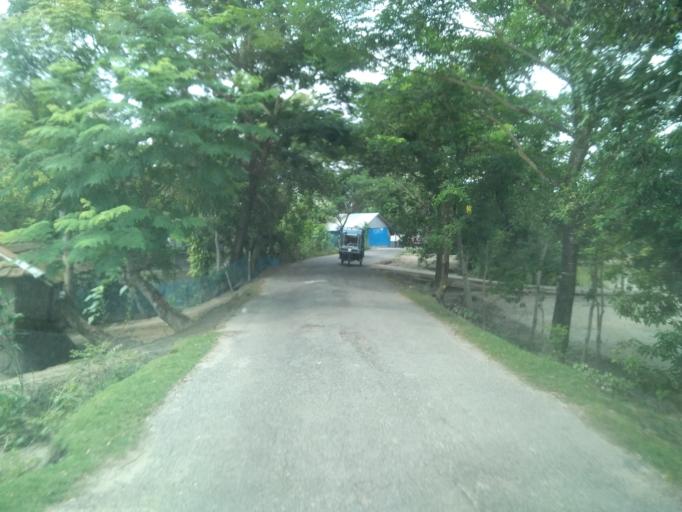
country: BD
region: Khulna
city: Phultala
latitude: 22.7021
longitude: 89.4560
